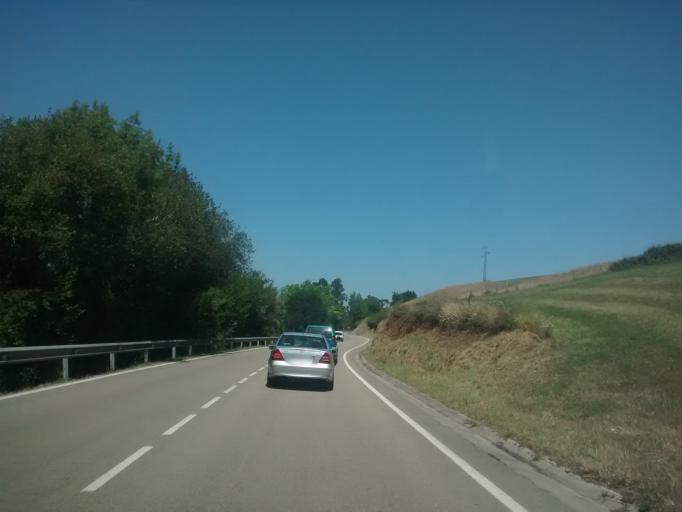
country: ES
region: Cantabria
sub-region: Provincia de Cantabria
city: San Miguel de Meruelo
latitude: 43.4659
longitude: -3.5857
